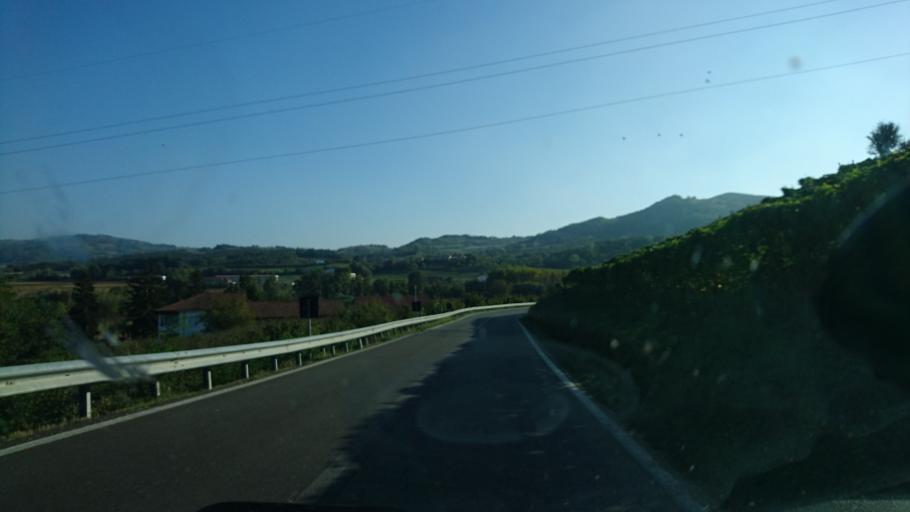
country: IT
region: Piedmont
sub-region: Provincia di Asti
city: Monastero Bormida
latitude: 44.6502
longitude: 8.3423
